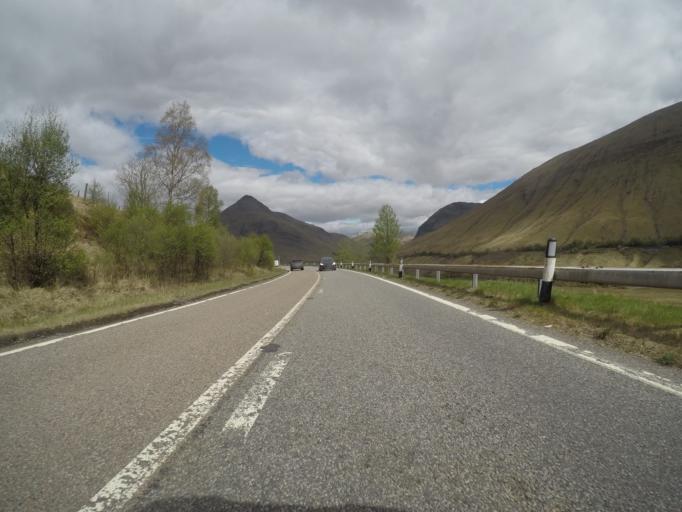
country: GB
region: Scotland
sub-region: Argyll and Bute
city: Garelochhead
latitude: 56.4678
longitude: -4.7248
